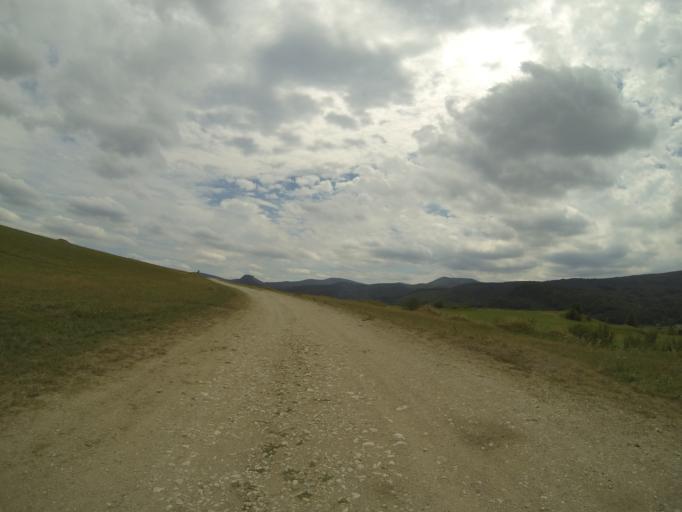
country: RO
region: Brasov
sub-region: Comuna Apata
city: Apata
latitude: 46.0274
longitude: 25.4197
